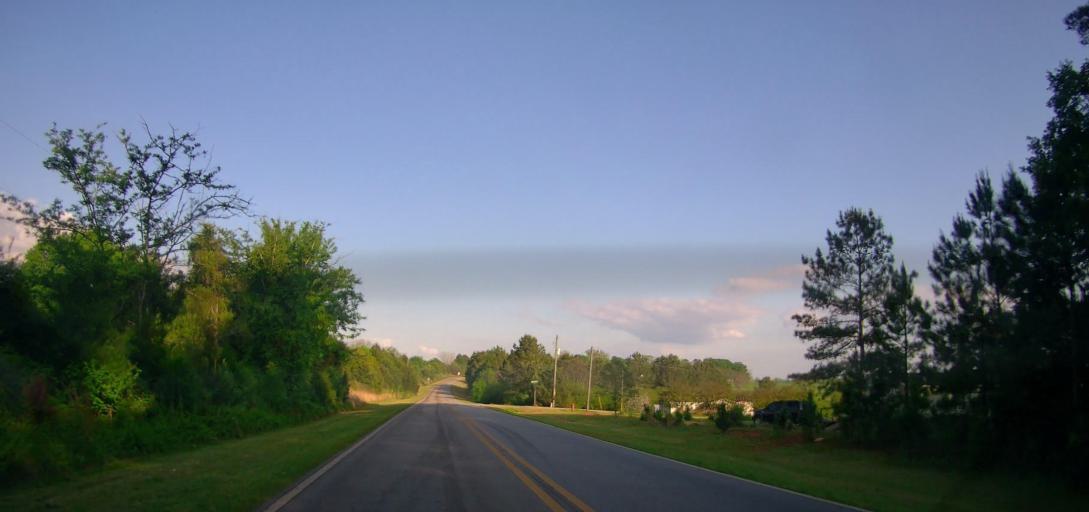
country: US
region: Georgia
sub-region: Putnam County
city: Eatonton
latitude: 33.3127
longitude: -83.3603
